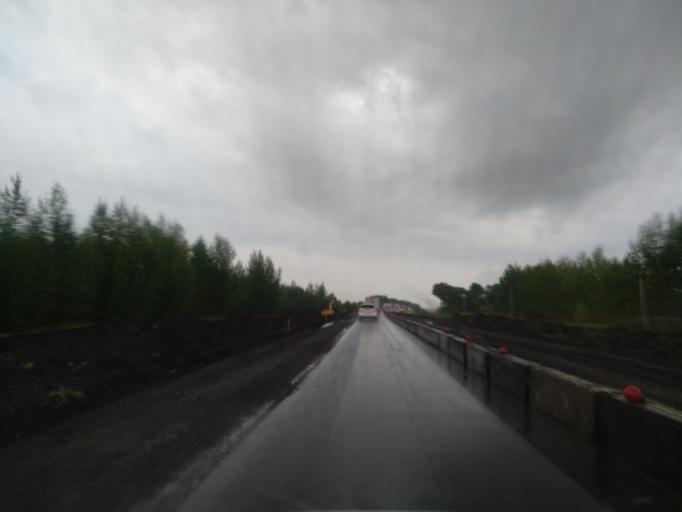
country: RU
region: Voronezj
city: Verkhnyaya Khava
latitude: 51.6762
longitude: 39.8398
